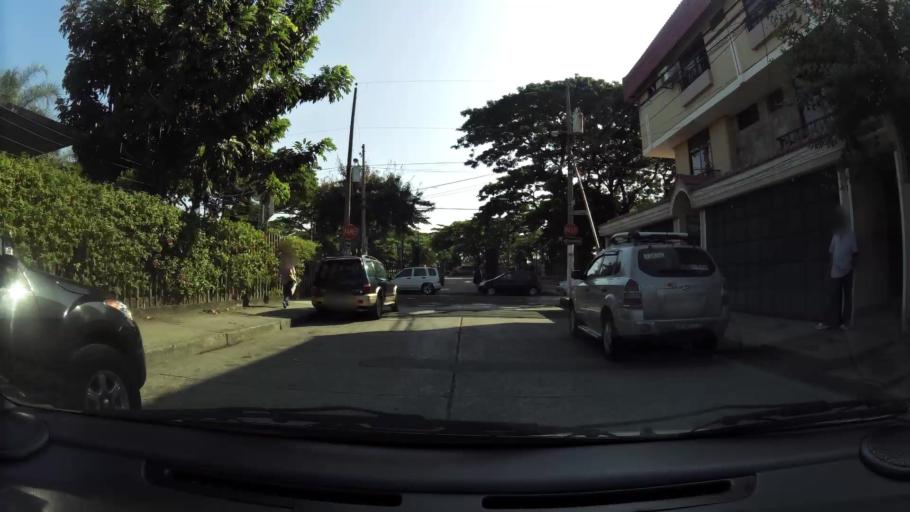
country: EC
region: Guayas
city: Guayaquil
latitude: -2.1763
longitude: -79.8990
